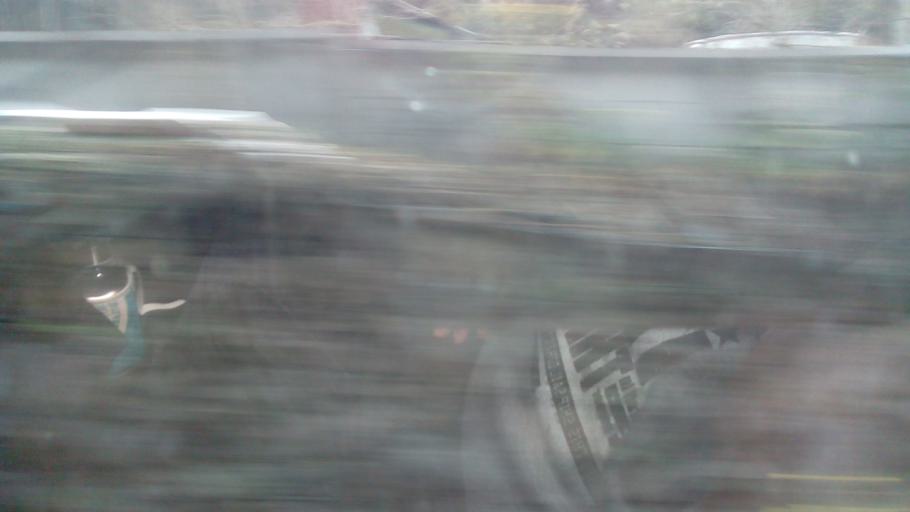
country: TW
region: Taiwan
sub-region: Hualien
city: Hualian
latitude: 24.3556
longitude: 121.3255
